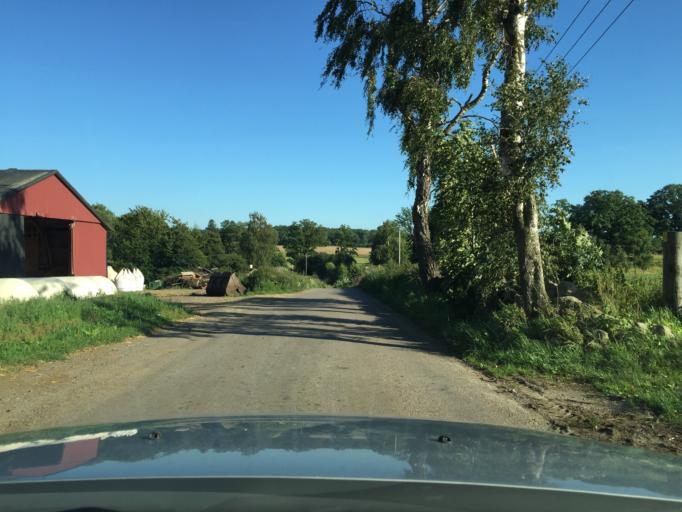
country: SE
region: Skane
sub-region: Hassleholms Kommun
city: Sosdala
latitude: 56.0397
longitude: 13.7303
